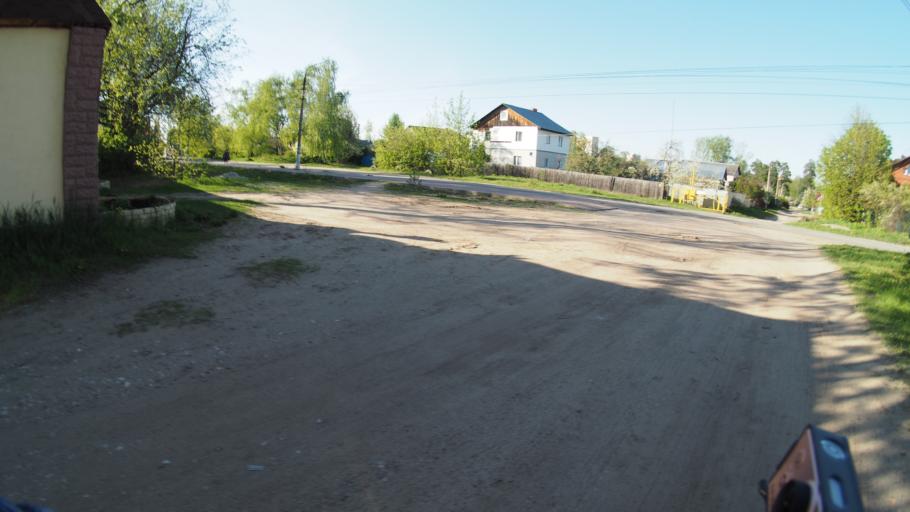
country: RU
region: Moskovskaya
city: Ramenskoye
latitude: 55.5560
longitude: 38.1951
